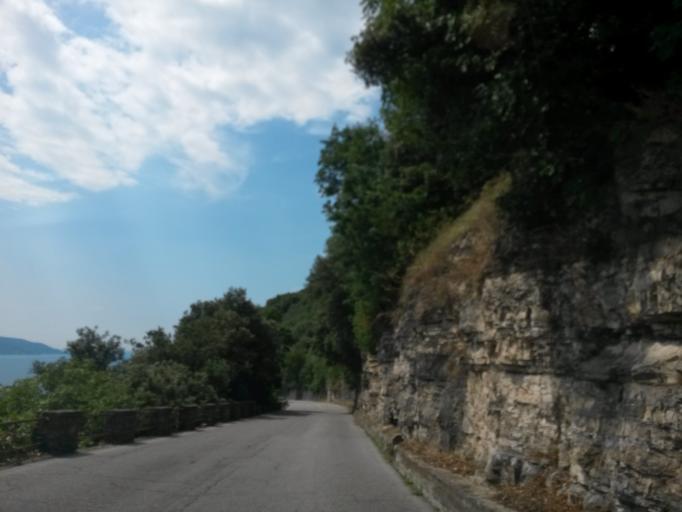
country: IT
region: Lombardy
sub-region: Provincia di Brescia
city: Gardola
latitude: 45.7148
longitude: 10.7016
